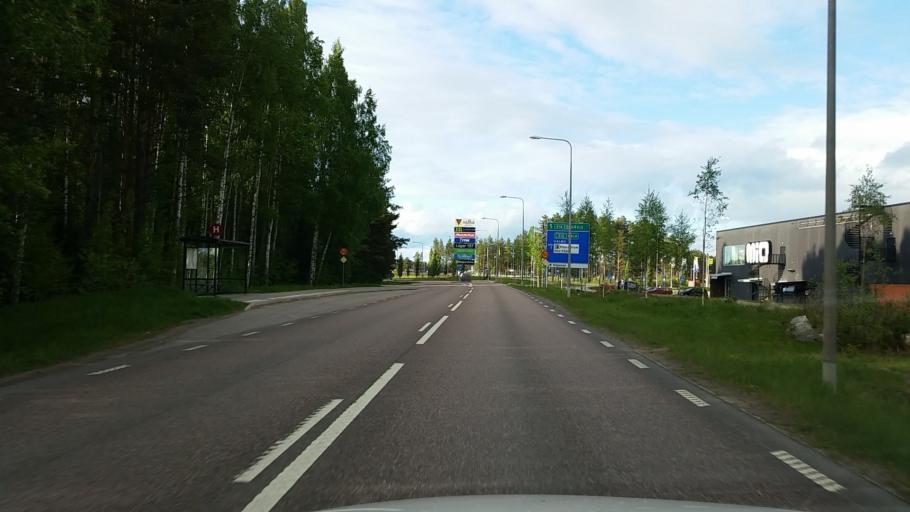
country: SE
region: Gaevleborg
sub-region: Gavle Kommun
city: Valbo
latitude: 60.6271
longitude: 16.9855
